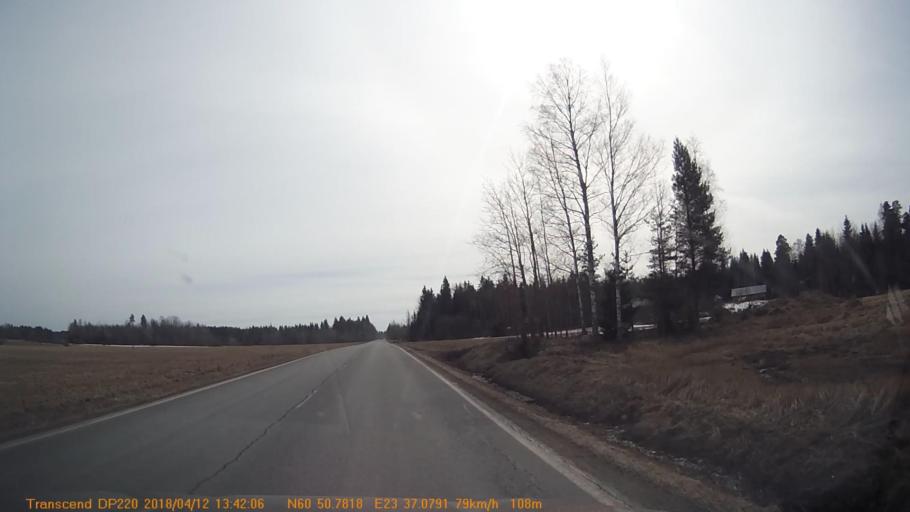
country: FI
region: Haeme
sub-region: Forssa
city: Forssa
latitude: 60.8456
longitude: 23.6180
